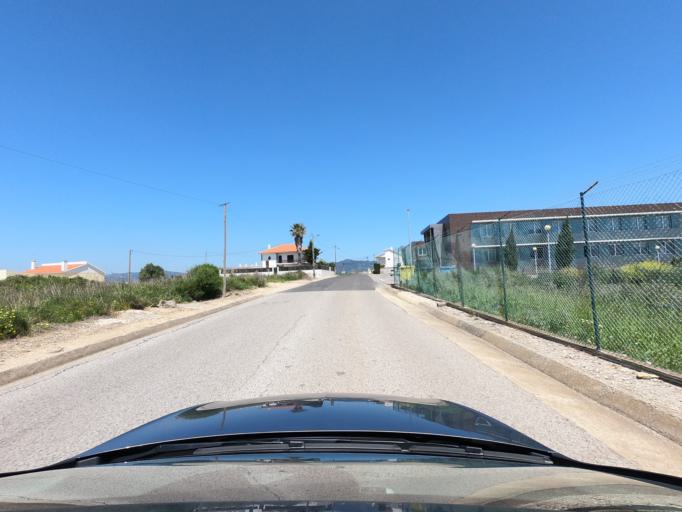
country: PT
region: Lisbon
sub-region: Cascais
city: Parede
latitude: 38.7246
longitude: -9.3595
